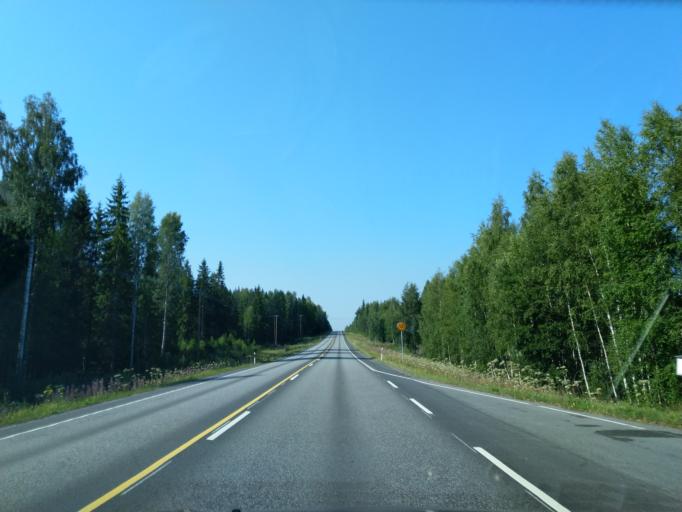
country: FI
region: Satakunta
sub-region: Pori
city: Pomarkku
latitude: 61.7274
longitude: 22.0659
